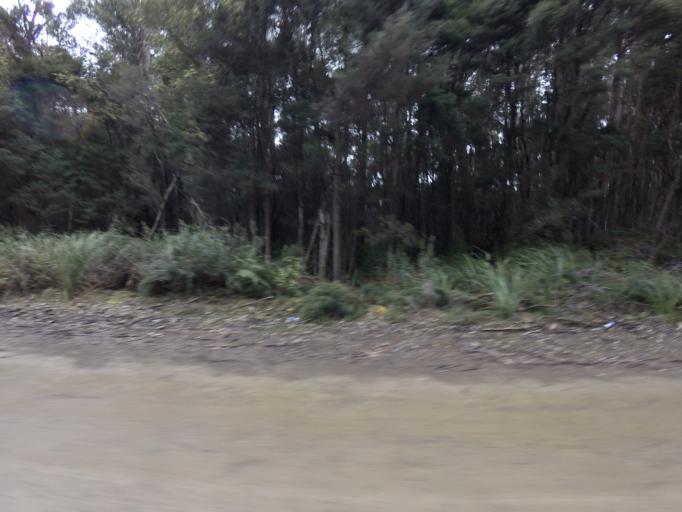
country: AU
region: Tasmania
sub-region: Huon Valley
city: Geeveston
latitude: -43.5132
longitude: 146.8852
